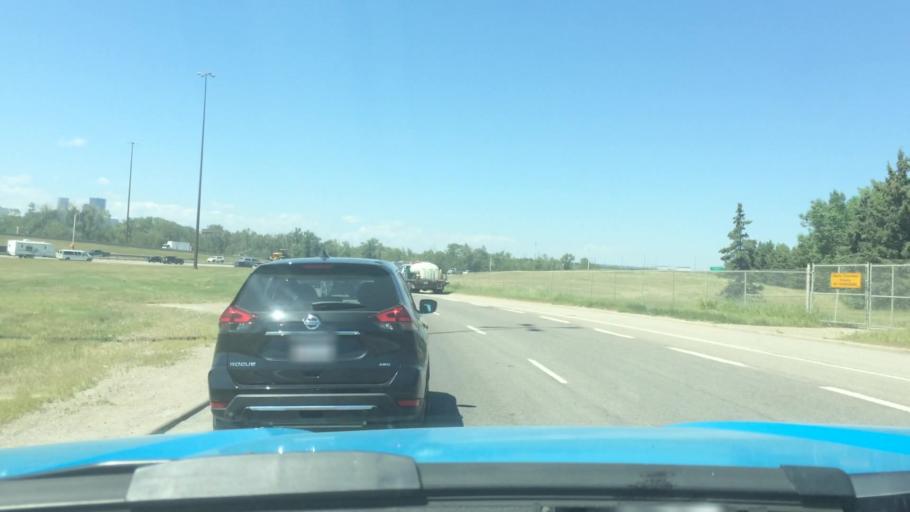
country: CA
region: Alberta
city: Calgary
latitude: 51.0383
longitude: -114.0035
